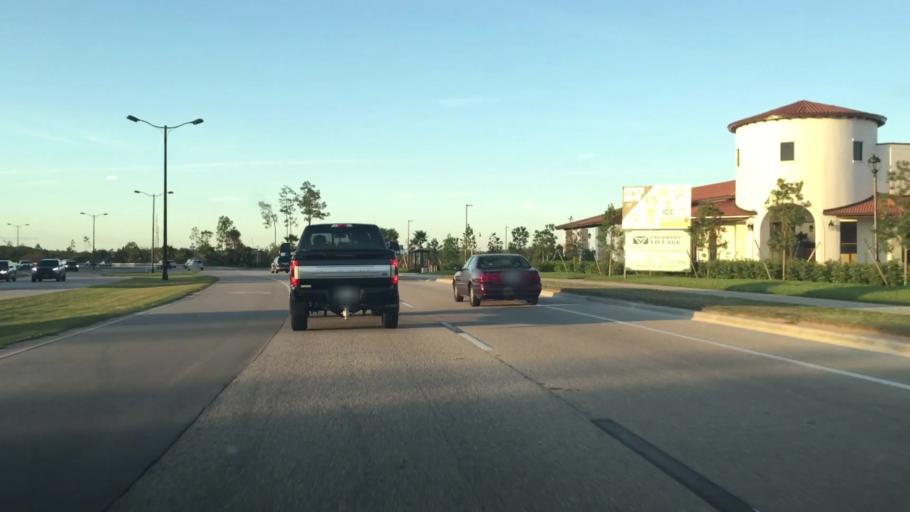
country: US
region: Florida
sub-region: Lee County
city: Three Oaks
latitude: 26.4518
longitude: -81.7744
